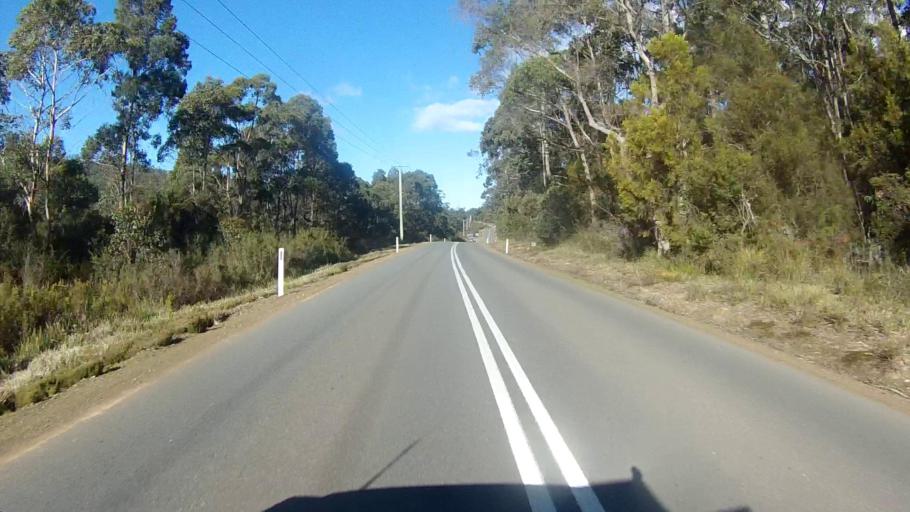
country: AU
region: Tasmania
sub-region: Clarence
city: Sandford
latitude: -43.0835
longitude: 147.8659
